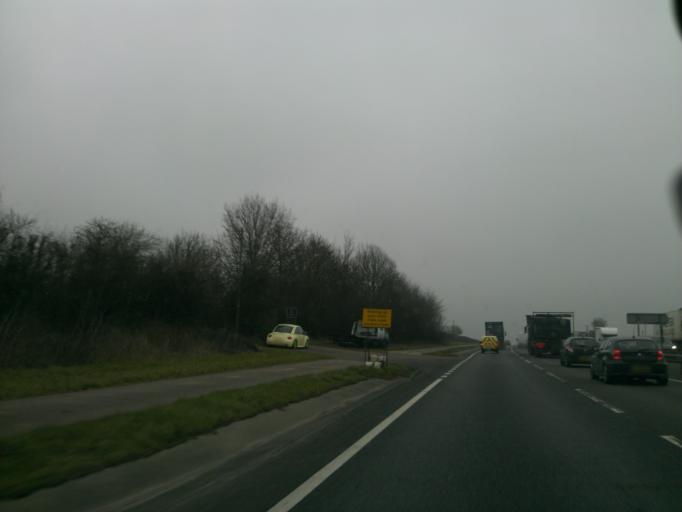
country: GB
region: England
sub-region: Essex
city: Marks Tey
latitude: 51.8564
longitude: 0.7396
